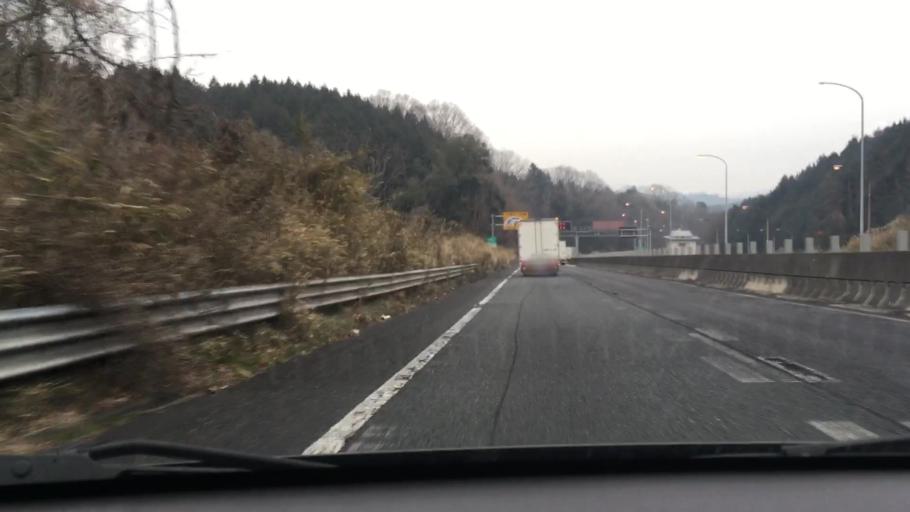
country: JP
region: Mie
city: Nabari
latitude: 34.6872
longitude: 136.0475
